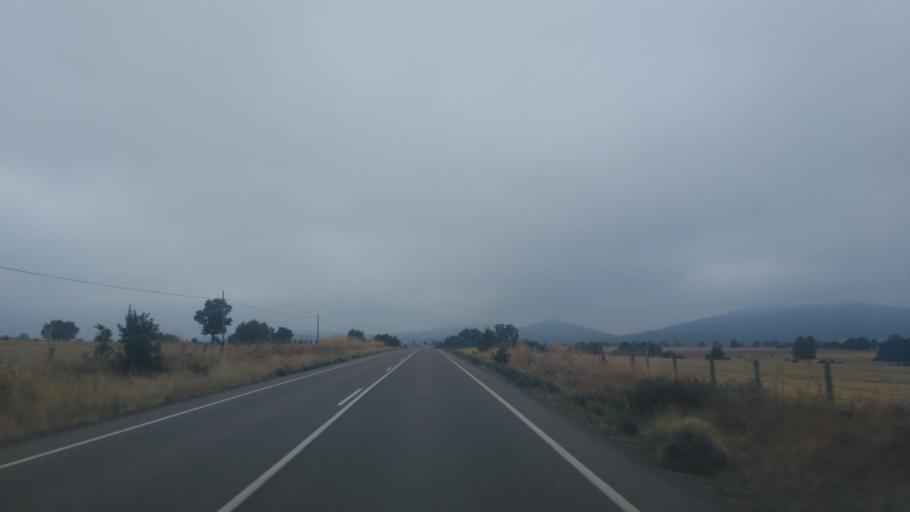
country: ES
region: Castille and Leon
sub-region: Provincia de Salamanca
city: Tamames
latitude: 40.6359
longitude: -6.1105
